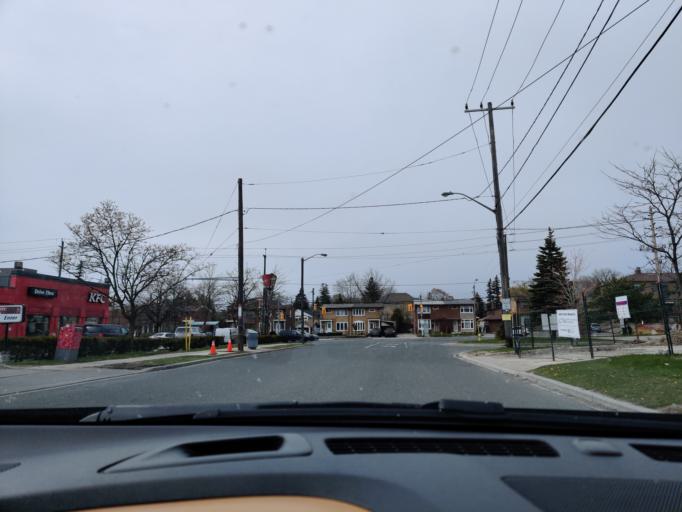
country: CA
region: Ontario
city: Toronto
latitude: 43.7096
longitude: -79.4716
